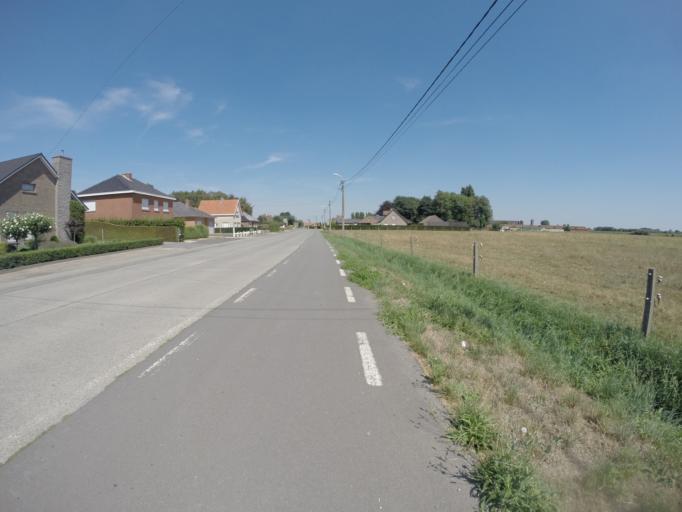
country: BE
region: Flanders
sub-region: Provincie Oost-Vlaanderen
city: Knesselare
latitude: 51.1187
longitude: 3.3964
